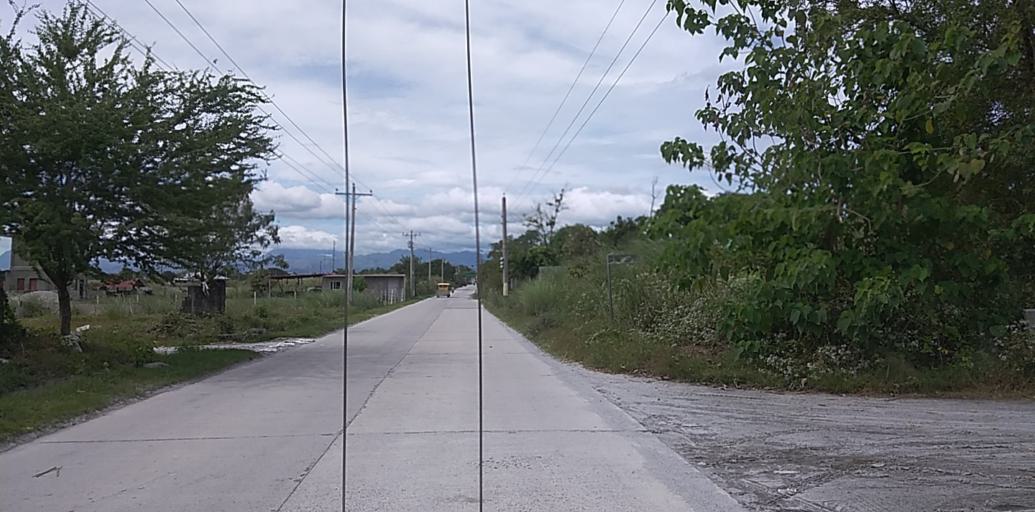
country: PH
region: Central Luzon
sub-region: Province of Pampanga
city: Balas
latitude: 15.0638
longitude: 120.5807
